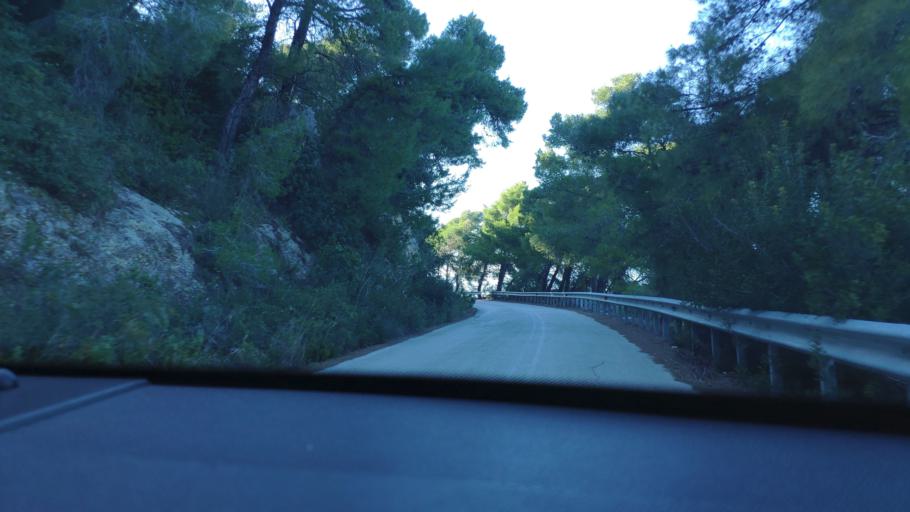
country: GR
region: Peloponnese
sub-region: Nomos Korinthias
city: Agioi Theodoroi
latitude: 38.0593
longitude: 23.1022
